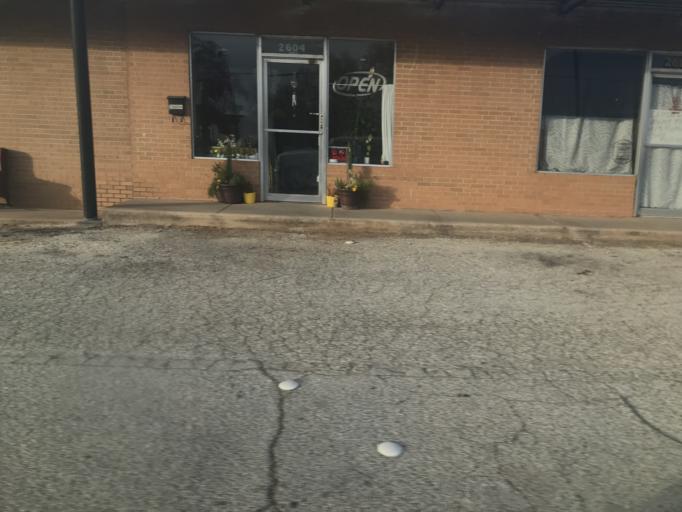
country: US
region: Texas
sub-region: Taylor County
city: Abilene
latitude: 32.4323
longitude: -99.7539
